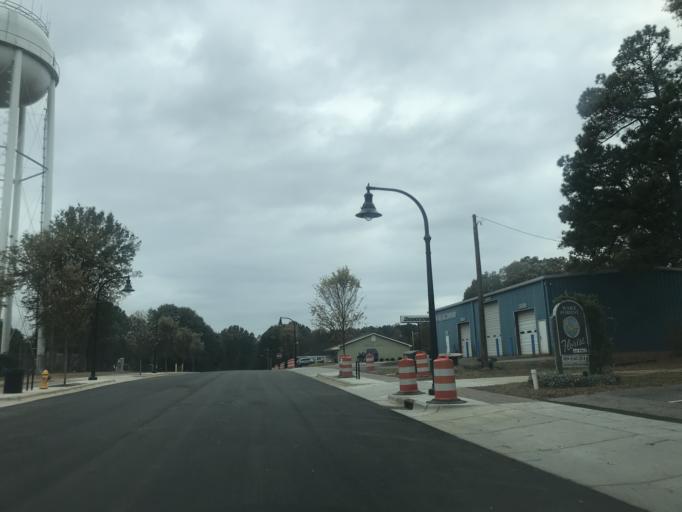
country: US
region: North Carolina
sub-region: Wake County
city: Wake Forest
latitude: 35.9727
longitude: -78.5123
